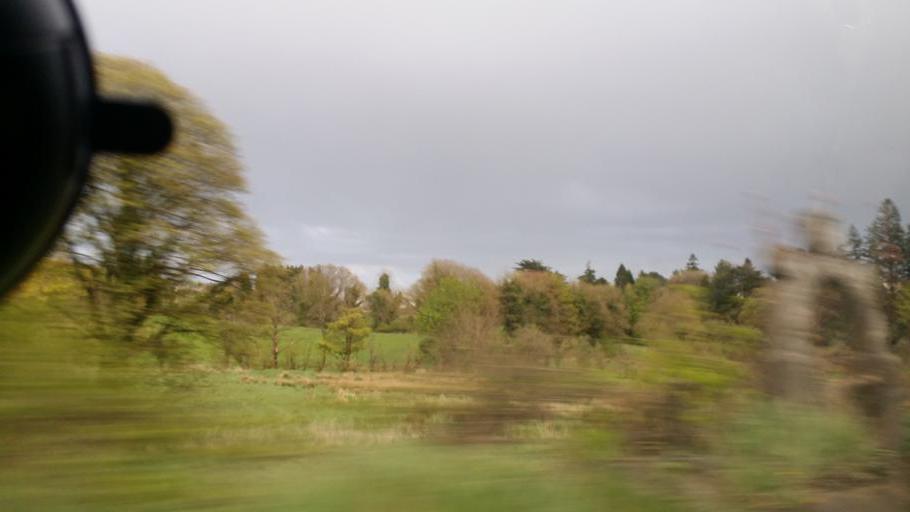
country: IE
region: Ulster
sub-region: An Cabhan
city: Virginia
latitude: 53.8486
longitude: -7.0999
